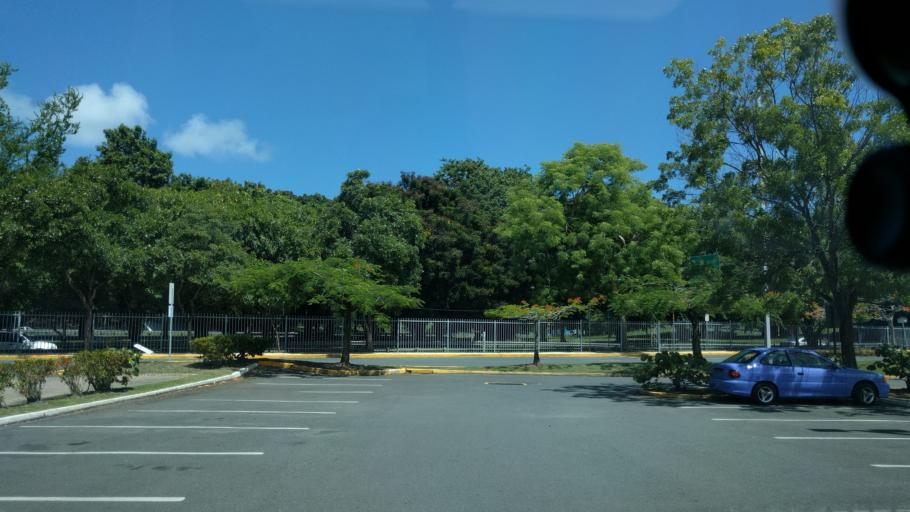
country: PR
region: San Juan
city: San Juan
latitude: 18.4418
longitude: -66.0787
